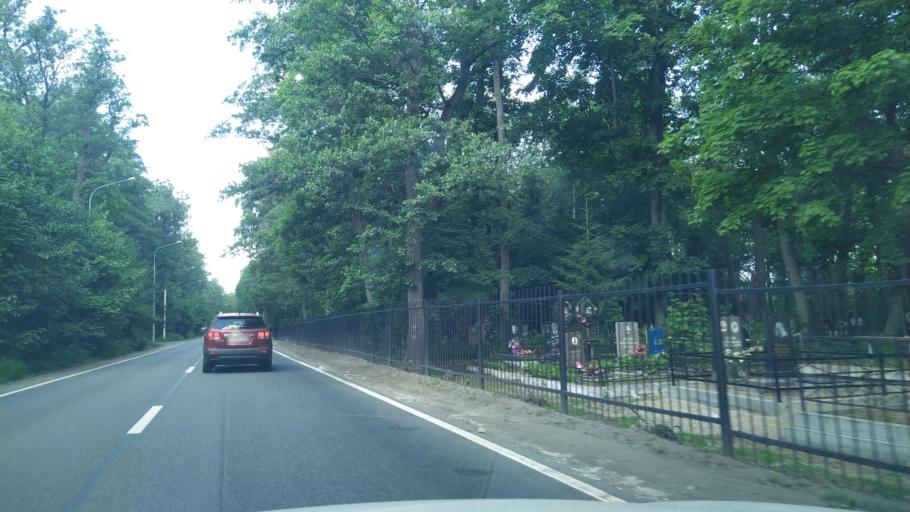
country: RU
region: St.-Petersburg
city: Kronshtadt
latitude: 60.0185
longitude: 29.7031
